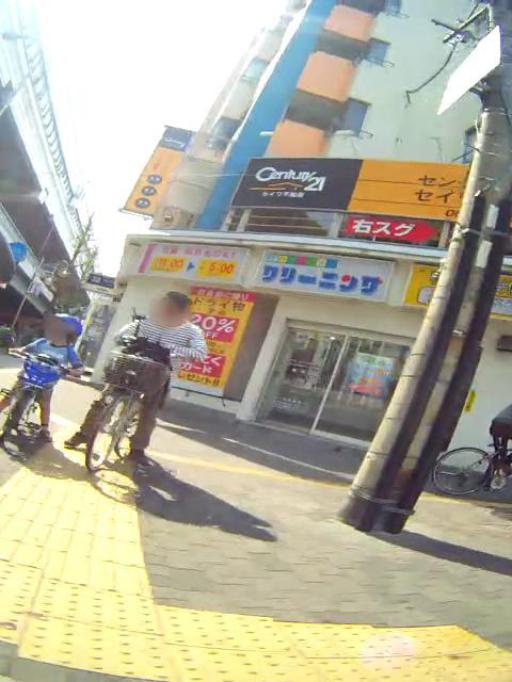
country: JP
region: Osaka
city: Osaka-shi
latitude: 34.6809
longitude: 135.5445
